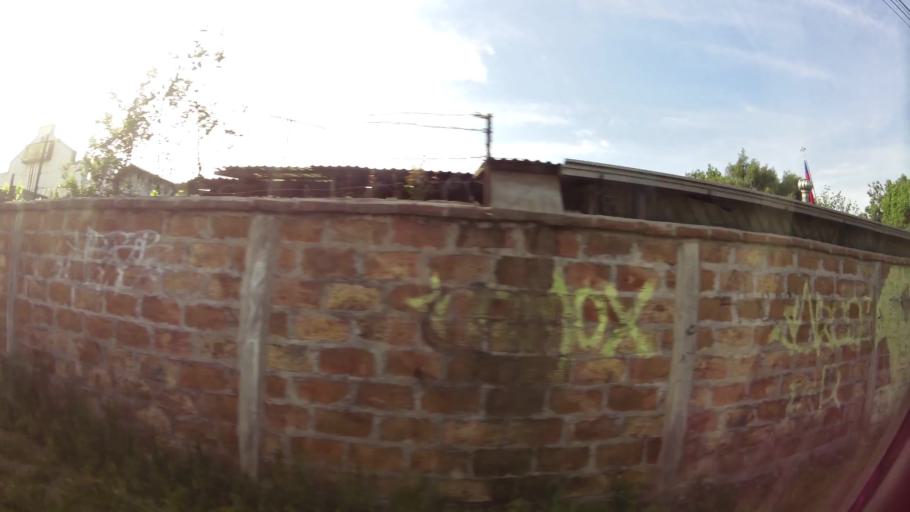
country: CL
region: Santiago Metropolitan
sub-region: Provincia de Talagante
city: Talagante
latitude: -33.6701
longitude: -70.9367
